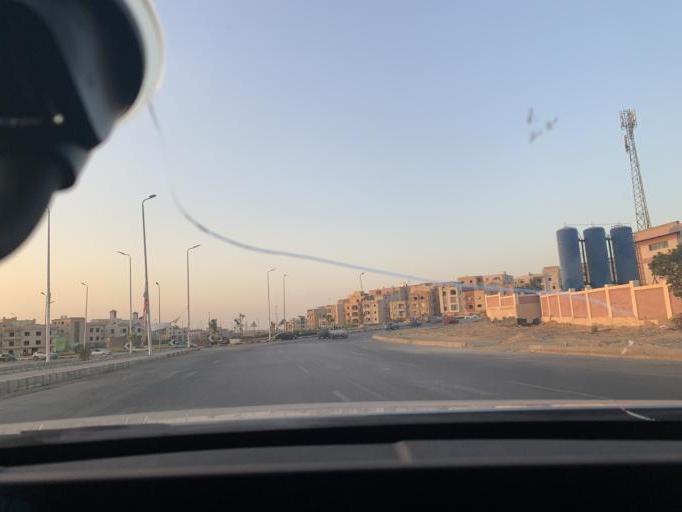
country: EG
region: Muhafazat al Qahirah
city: Cairo
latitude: 29.9979
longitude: 31.4689
